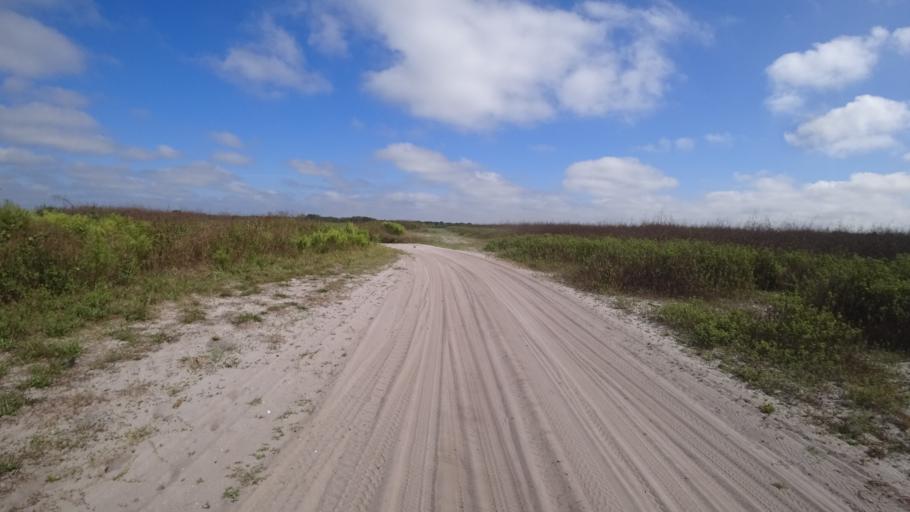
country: US
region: Florida
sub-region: DeSoto County
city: Arcadia
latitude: 27.2889
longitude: -82.0748
